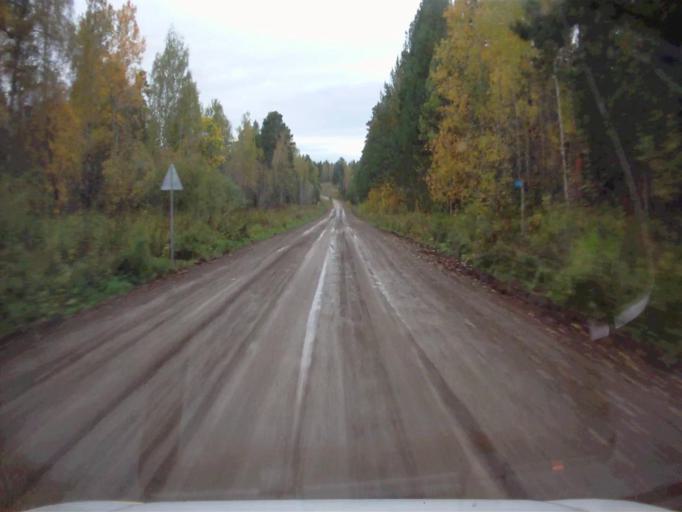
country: RU
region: Chelyabinsk
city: Nyazepetrovsk
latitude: 56.0873
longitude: 59.4174
